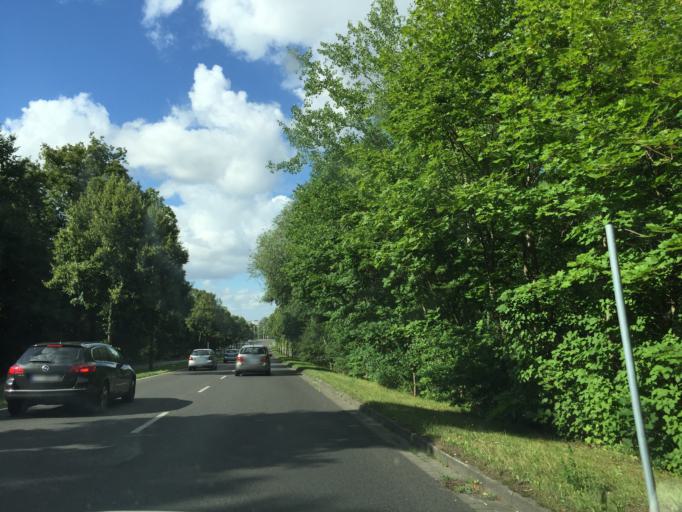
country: DE
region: Mecklenburg-Vorpommern
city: Neubrandenburg
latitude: 53.5331
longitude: 13.2631
